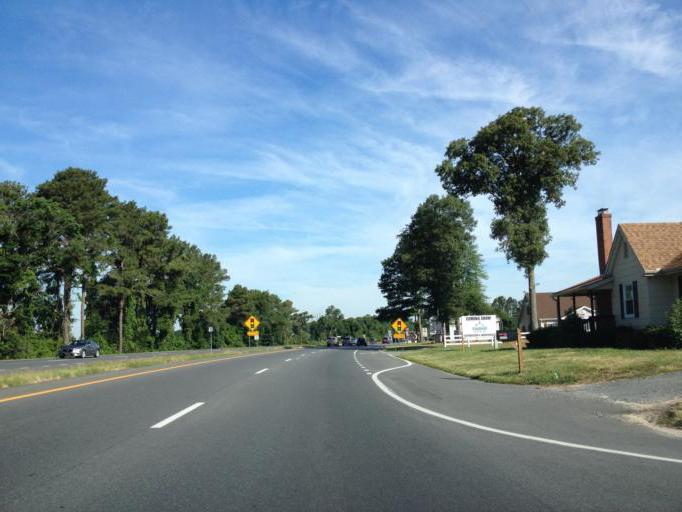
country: US
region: Delaware
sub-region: Sussex County
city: Millsboro
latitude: 38.5962
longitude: -75.3140
